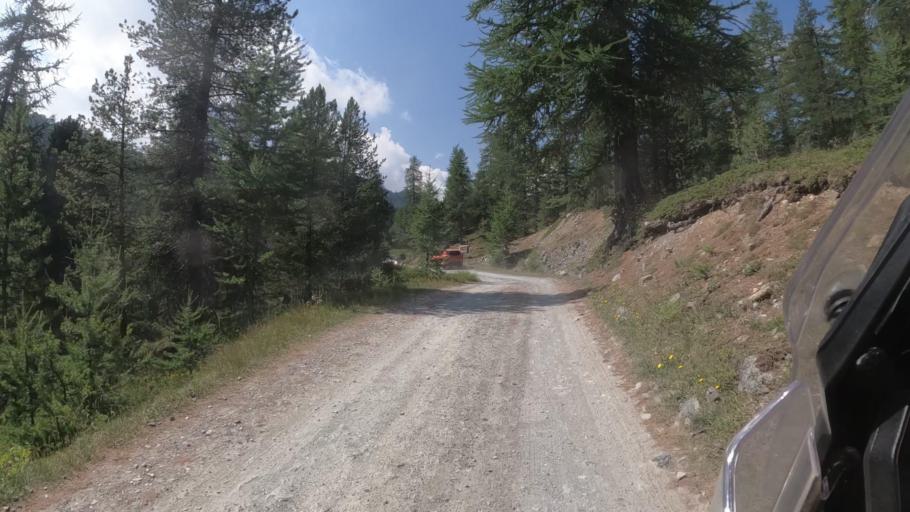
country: IT
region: Piedmont
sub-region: Provincia di Torino
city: Cesana Torinese
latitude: 44.9088
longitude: 6.7994
